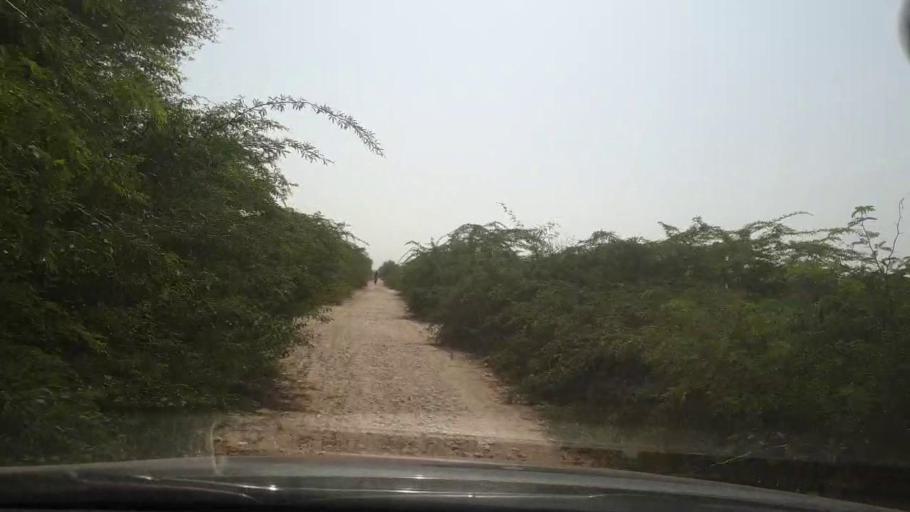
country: PK
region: Sindh
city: Naukot
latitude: 24.7943
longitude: 69.2129
